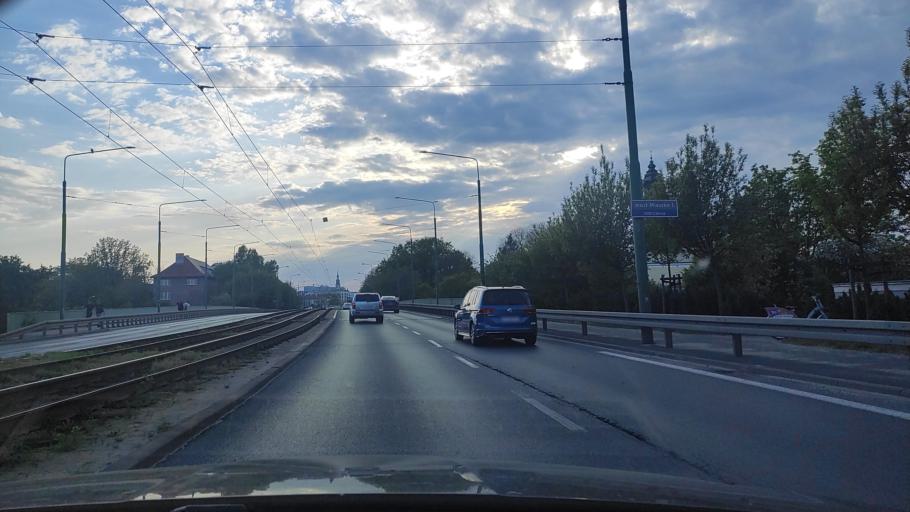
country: PL
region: Greater Poland Voivodeship
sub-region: Poznan
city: Poznan
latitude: 52.4110
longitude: 16.9530
